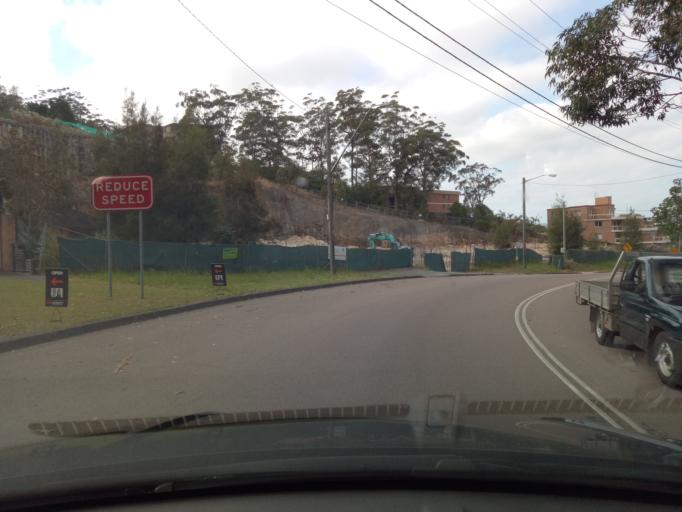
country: AU
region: New South Wales
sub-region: Gosford Shire
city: Gosford
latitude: -33.4314
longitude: 151.3438
